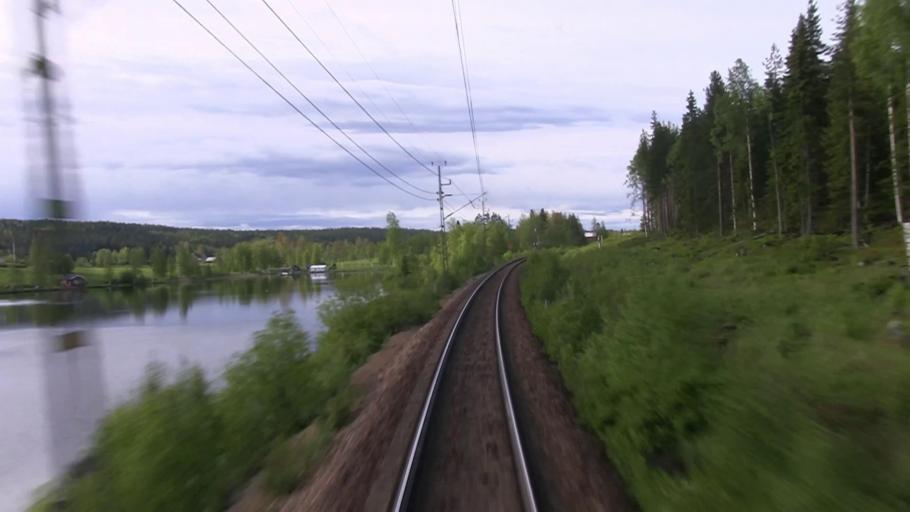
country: SE
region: Vaesterbotten
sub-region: Vindelns Kommun
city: Vindeln
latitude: 64.1124
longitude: 19.6904
